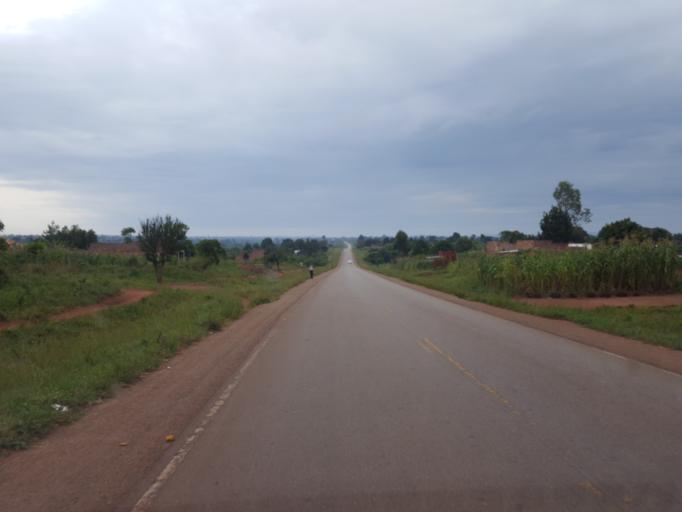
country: UG
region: Central Region
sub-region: Kyankwanzi District
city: Kyankwanzi
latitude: 1.1112
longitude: 31.6112
